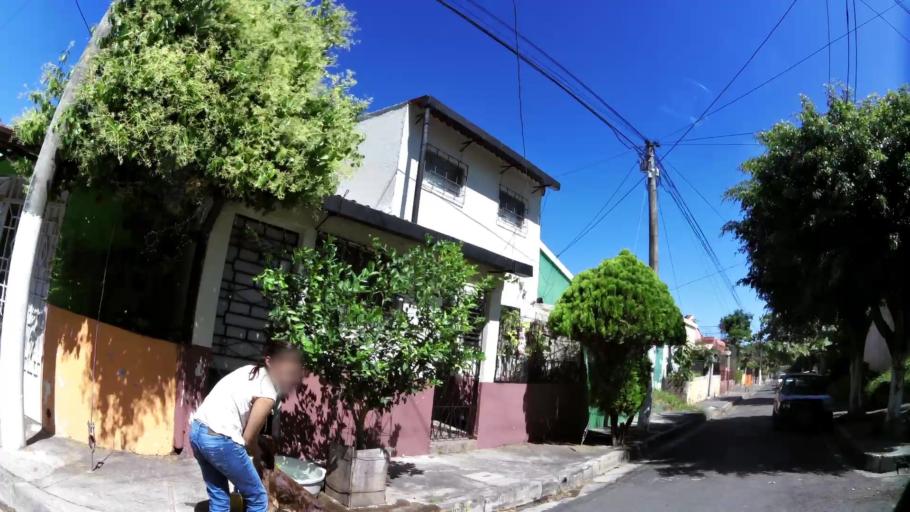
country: SV
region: La Libertad
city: Santa Tecla
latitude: 13.6724
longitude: -89.3028
